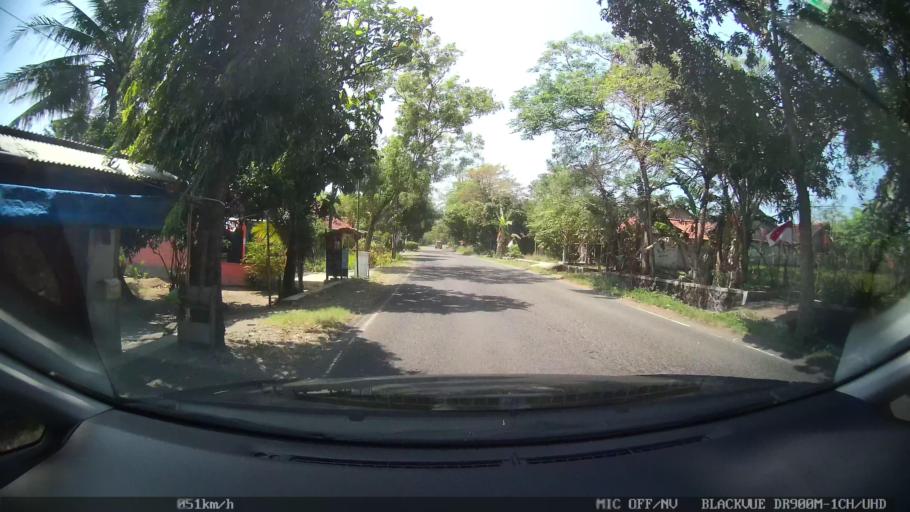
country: ID
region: Daerah Istimewa Yogyakarta
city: Srandakan
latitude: -7.9145
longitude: 110.0967
